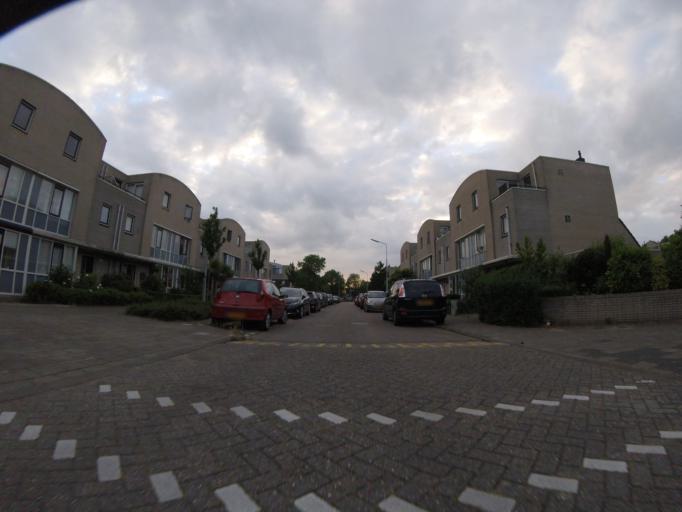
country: NL
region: North Holland
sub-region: Gemeente Haarlemmermeer
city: Hoofddorp
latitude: 52.2952
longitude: 4.6692
